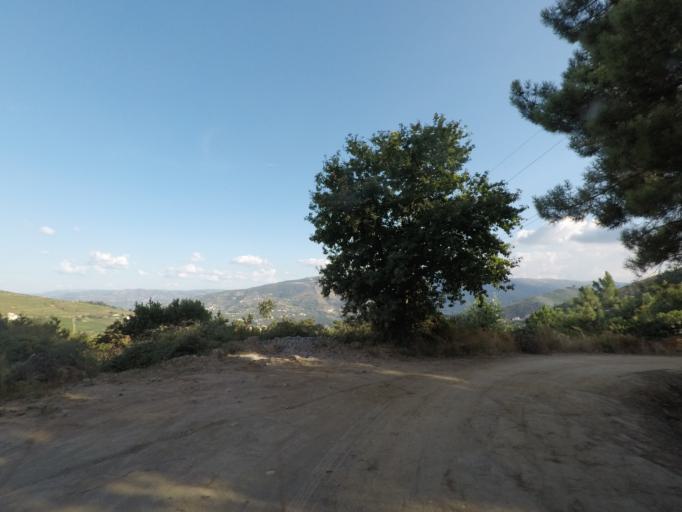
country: PT
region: Vila Real
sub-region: Mesao Frio
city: Mesao Frio
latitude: 41.1701
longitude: -7.9036
